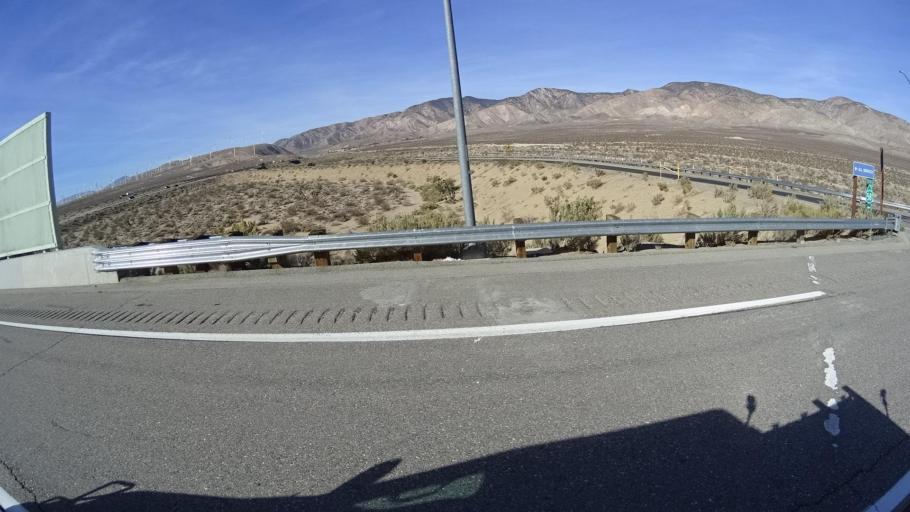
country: US
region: California
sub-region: Kern County
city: Mojave
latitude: 35.1154
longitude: -118.1785
